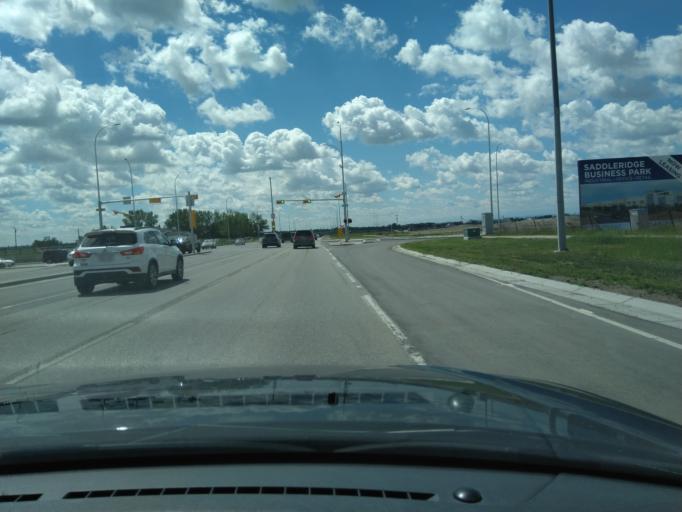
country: CA
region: Alberta
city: Calgary
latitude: 51.1332
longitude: -113.9702
